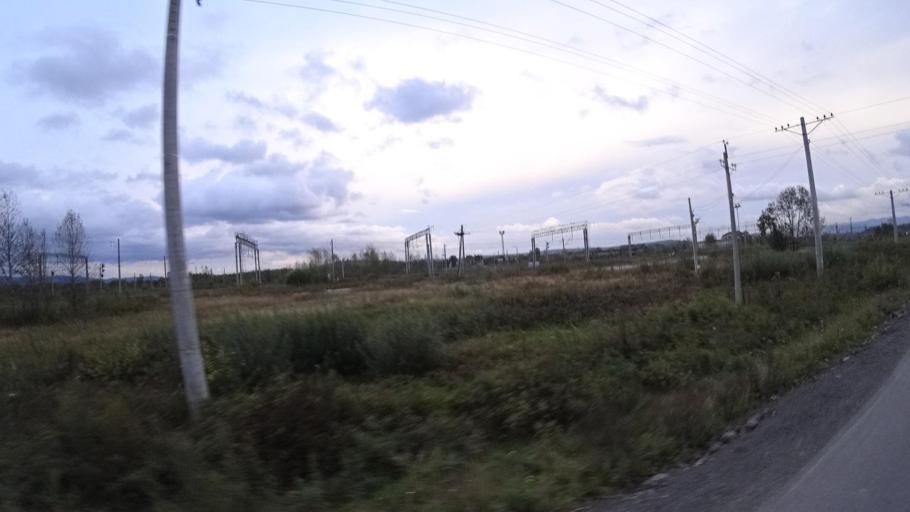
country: RU
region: Jewish Autonomous Oblast
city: Izvestkovyy
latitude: 48.9880
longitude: 131.5442
